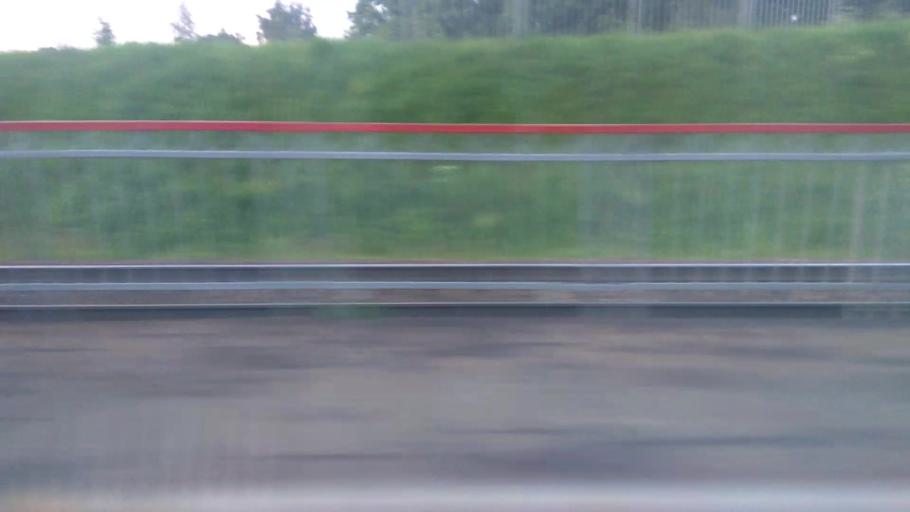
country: RU
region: Moskovskaya
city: Vostryakovo
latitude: 55.3827
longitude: 37.8145
